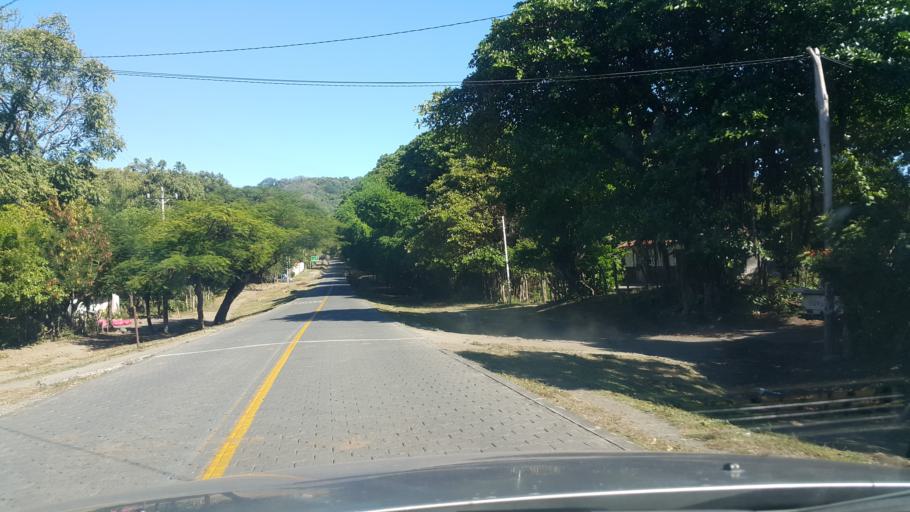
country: NI
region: Rivas
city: Moyogalpa
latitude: 11.4860
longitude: -85.6404
